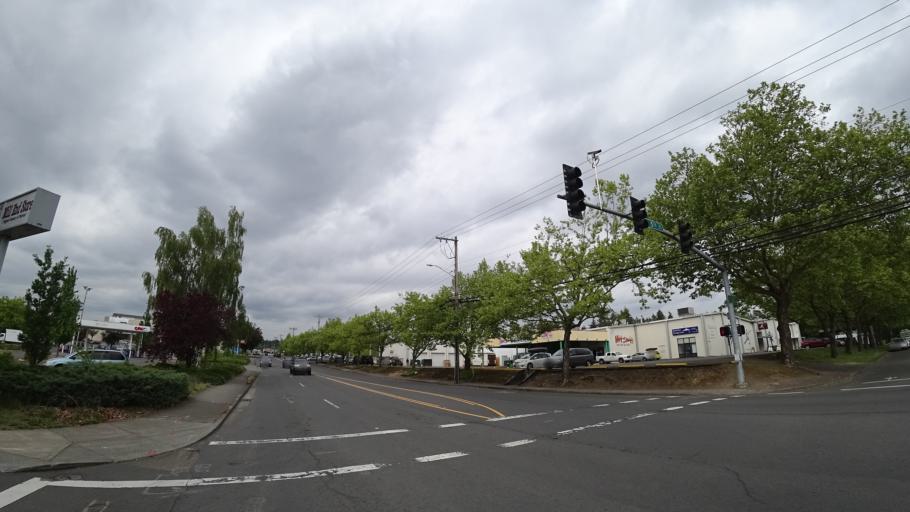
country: US
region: Oregon
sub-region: Washington County
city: Raleigh Hills
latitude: 45.4838
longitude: -122.7828
